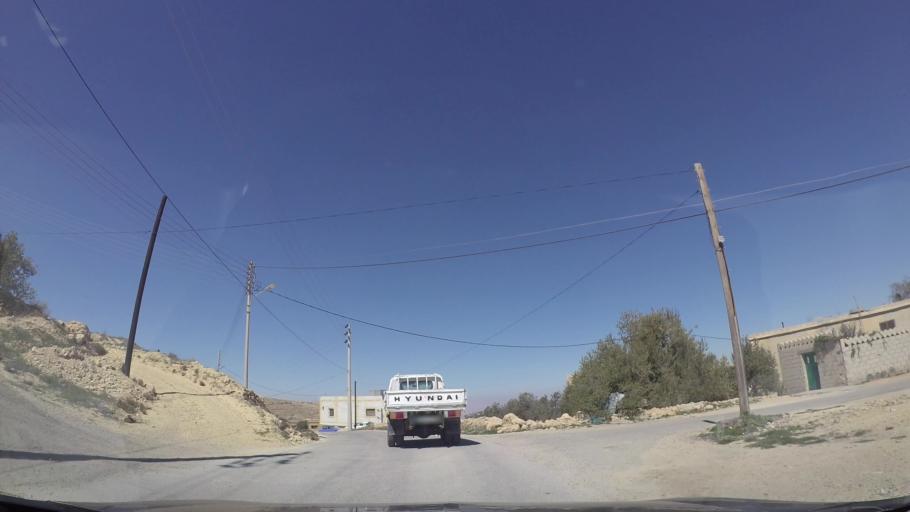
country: JO
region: Tafielah
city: At Tafilah
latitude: 30.8386
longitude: 35.5740
